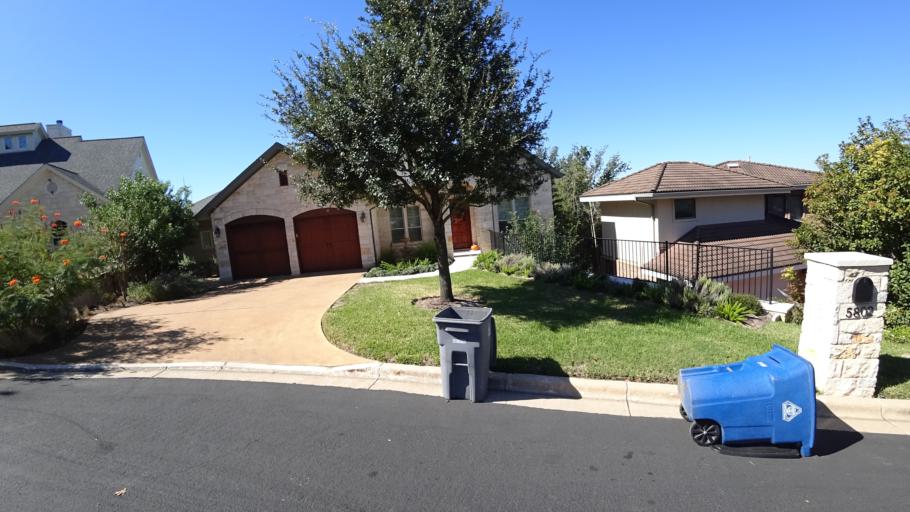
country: US
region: Texas
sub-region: Travis County
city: West Lake Hills
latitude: 30.3448
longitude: -97.7835
